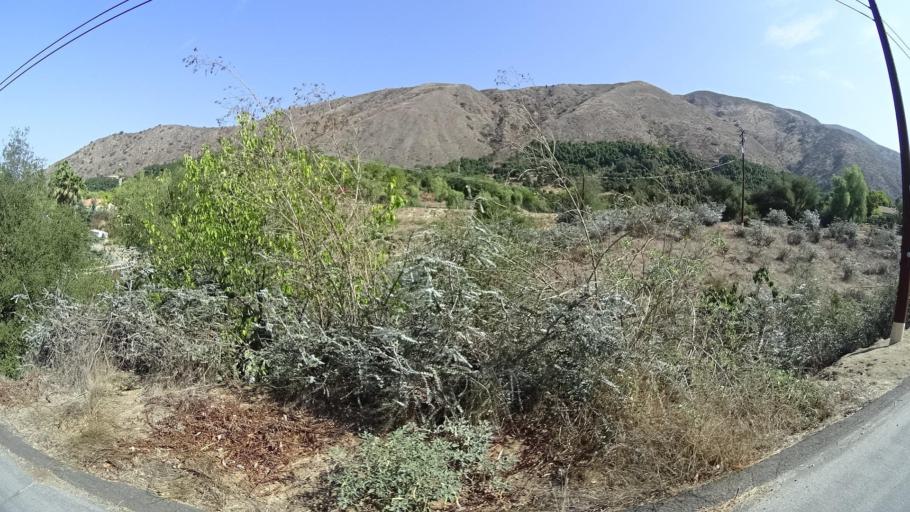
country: US
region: California
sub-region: San Diego County
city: Valley Center
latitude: 33.3421
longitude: -116.9988
